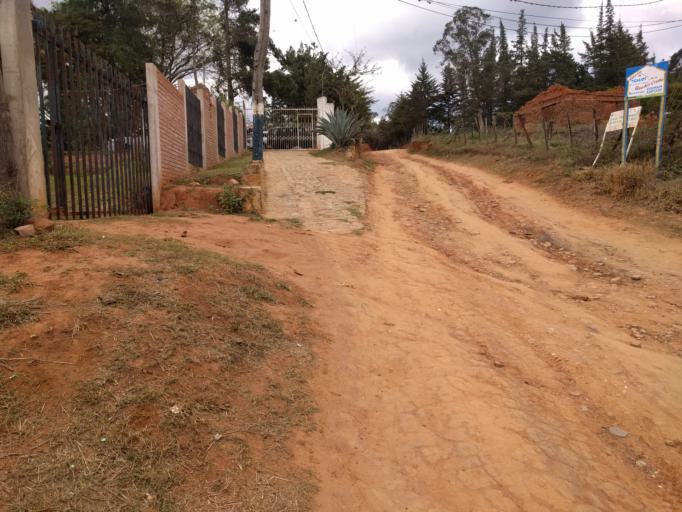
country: BO
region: Santa Cruz
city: Samaipata
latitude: -18.1832
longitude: -63.8771
